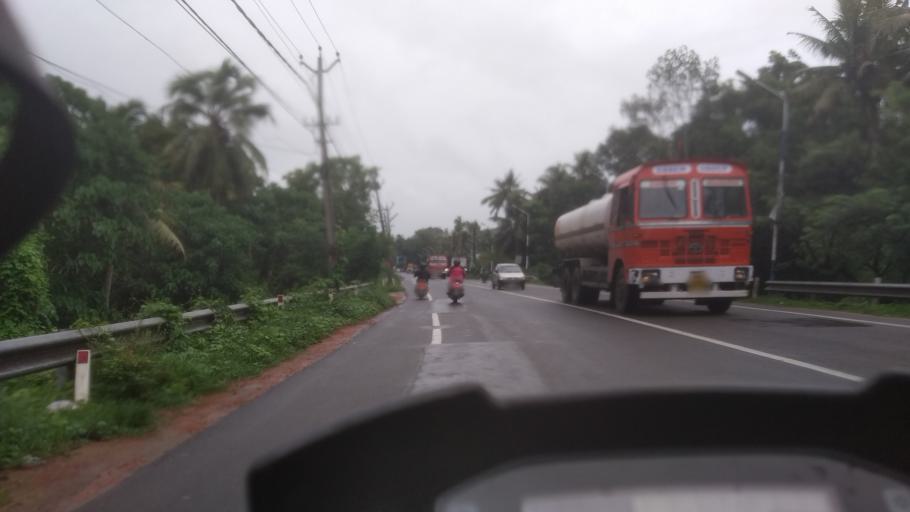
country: IN
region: Kerala
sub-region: Alappuzha
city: Kayankulam
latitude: 9.1522
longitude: 76.5123
